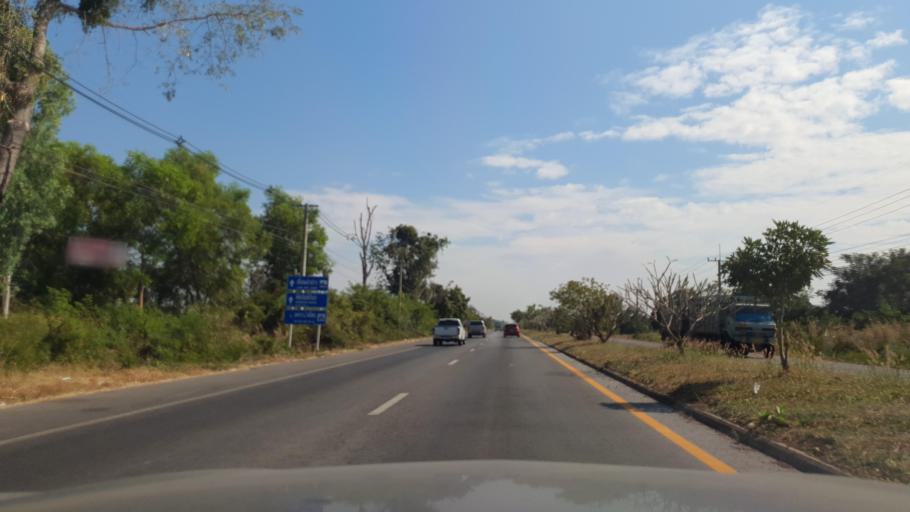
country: TH
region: Maha Sarakham
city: Chiang Yuen
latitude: 16.3803
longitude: 103.1991
